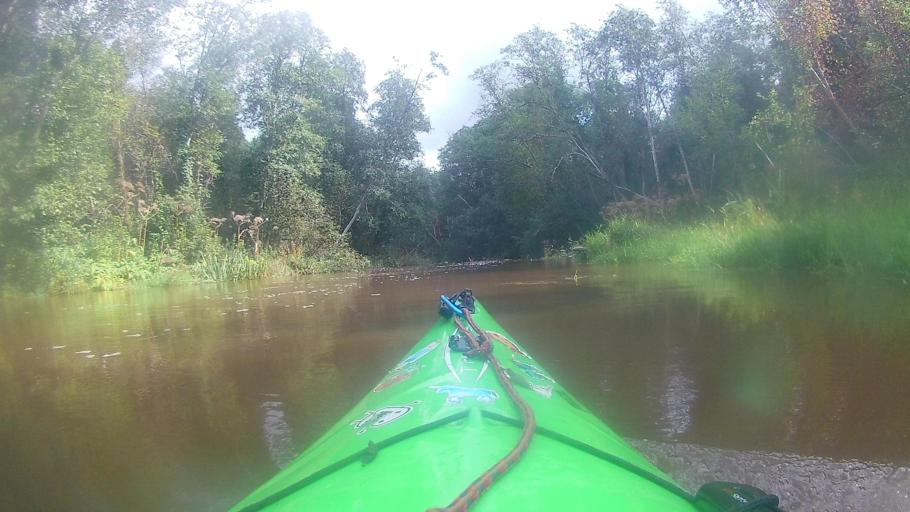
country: LV
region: Talsu Rajons
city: Sabile
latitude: 57.0026
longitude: 22.6140
